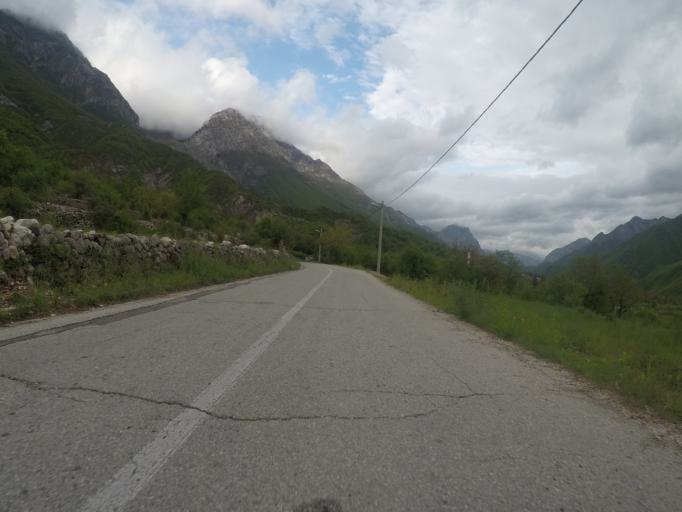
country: BA
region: Federation of Bosnia and Herzegovina
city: Siroki Brijeg
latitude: 43.5423
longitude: 17.5681
